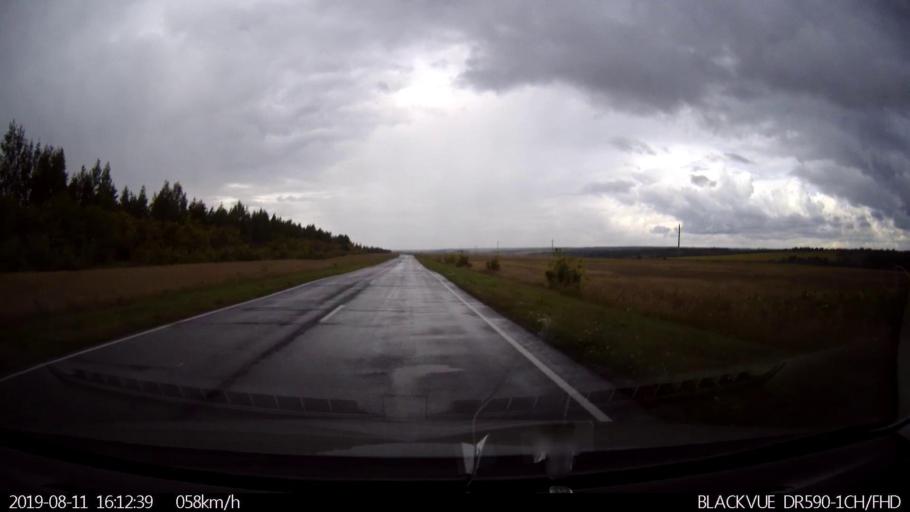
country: RU
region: Ulyanovsk
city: Ignatovka
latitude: 54.0131
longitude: 47.6398
